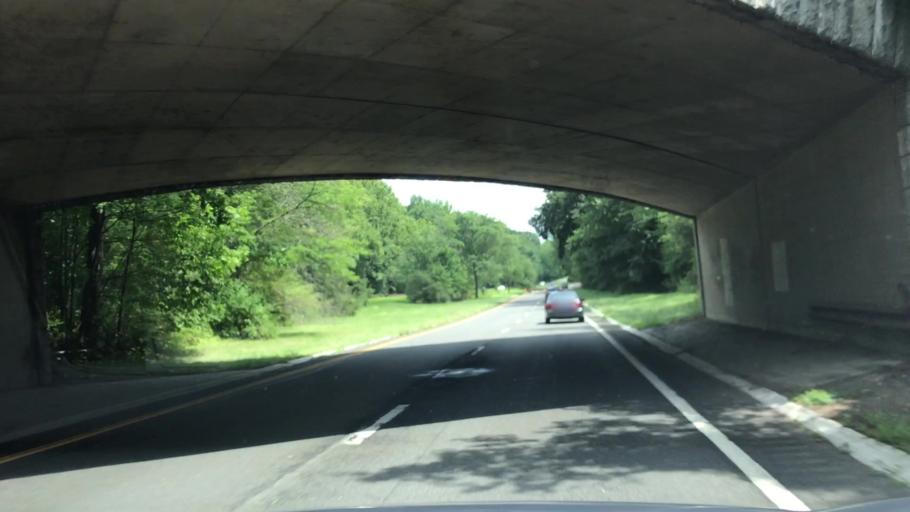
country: US
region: New York
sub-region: Rockland County
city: Blauvelt
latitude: 41.0589
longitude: -73.9709
